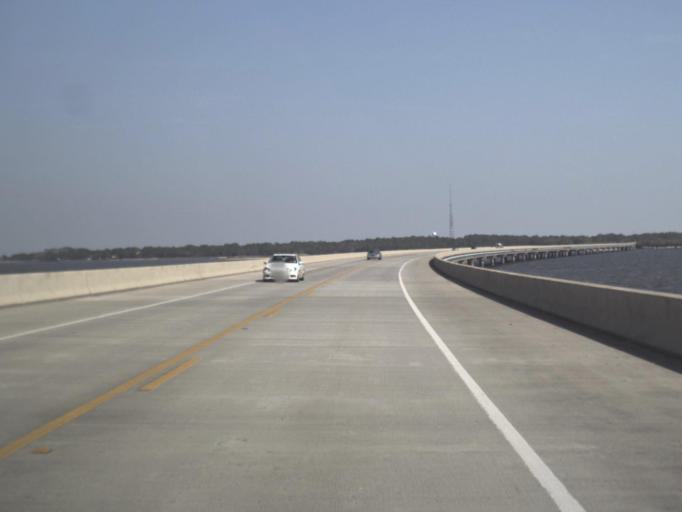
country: US
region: Florida
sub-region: Franklin County
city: Eastpoint
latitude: 29.7118
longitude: -84.8909
